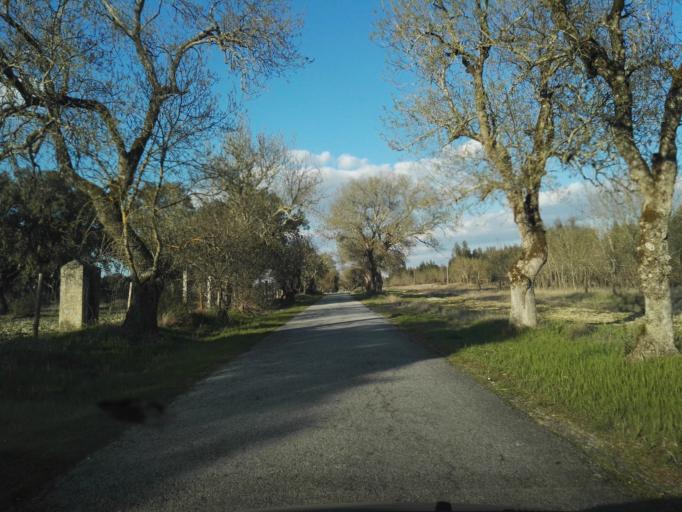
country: PT
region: Evora
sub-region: Evora
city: Evora
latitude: 38.5447
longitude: -7.9365
